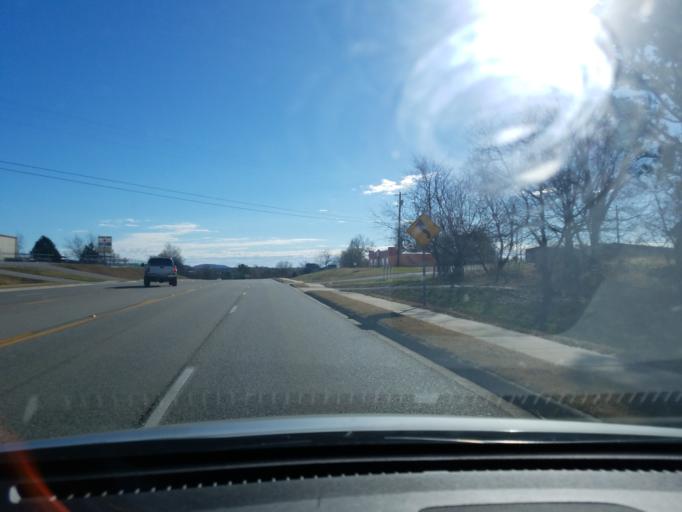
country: US
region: Arkansas
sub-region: Carroll County
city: Berryville
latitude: 36.3835
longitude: -93.6023
